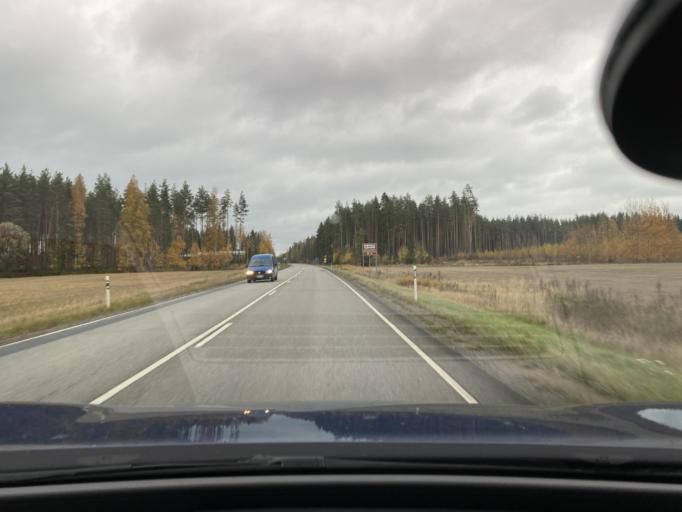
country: FI
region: Varsinais-Suomi
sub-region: Loimaa
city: Ylaene
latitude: 60.8874
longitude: 22.4025
